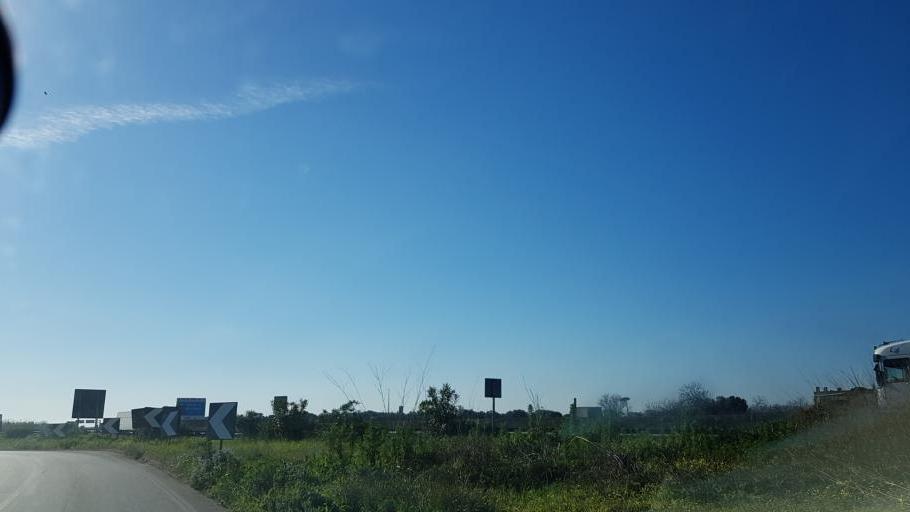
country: IT
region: Apulia
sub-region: Provincia di Brindisi
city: Brindisi
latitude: 40.6512
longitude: 17.9091
